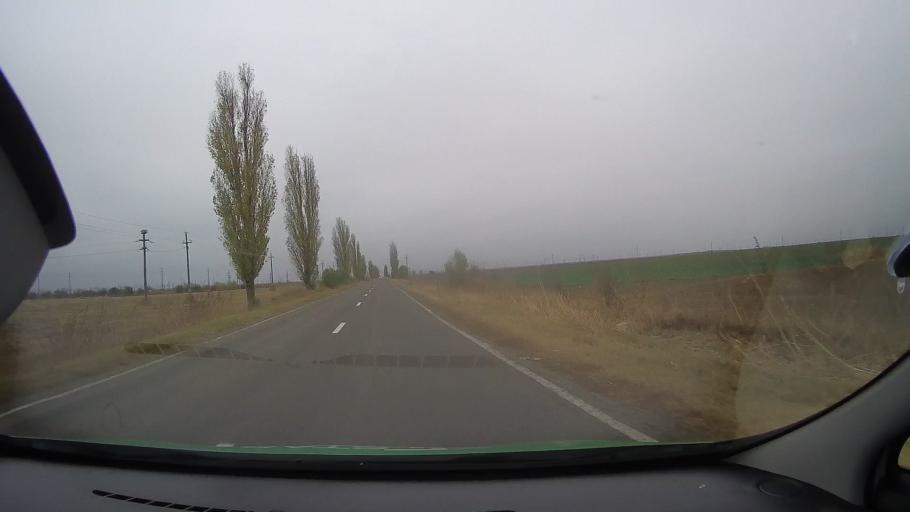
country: RO
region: Ialomita
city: Tandarei
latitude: 44.6593
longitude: 27.6466
